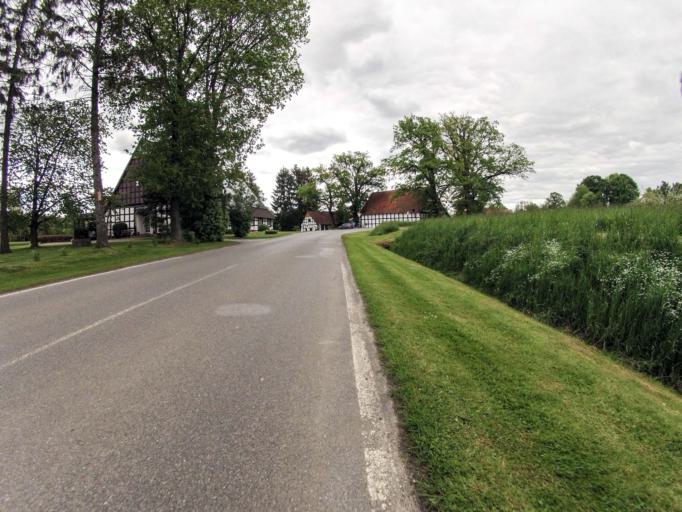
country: DE
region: Lower Saxony
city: Laar
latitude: 52.3313
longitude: 8.2591
